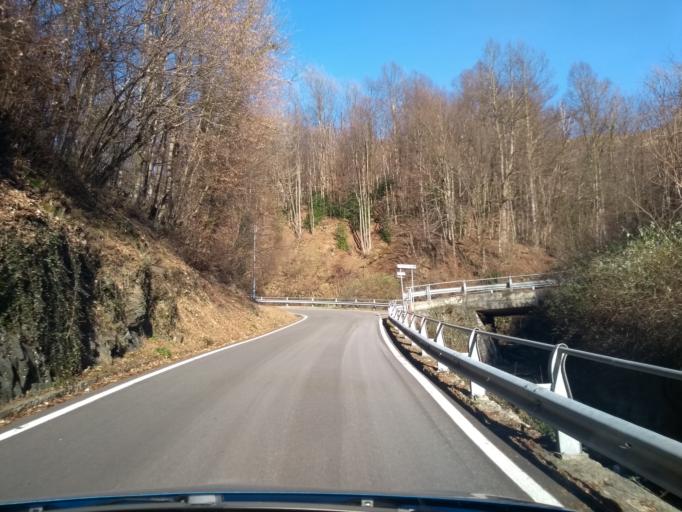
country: IT
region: Piedmont
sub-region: Provincia di Torino
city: Pessinetto
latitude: 45.2848
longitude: 7.4177
